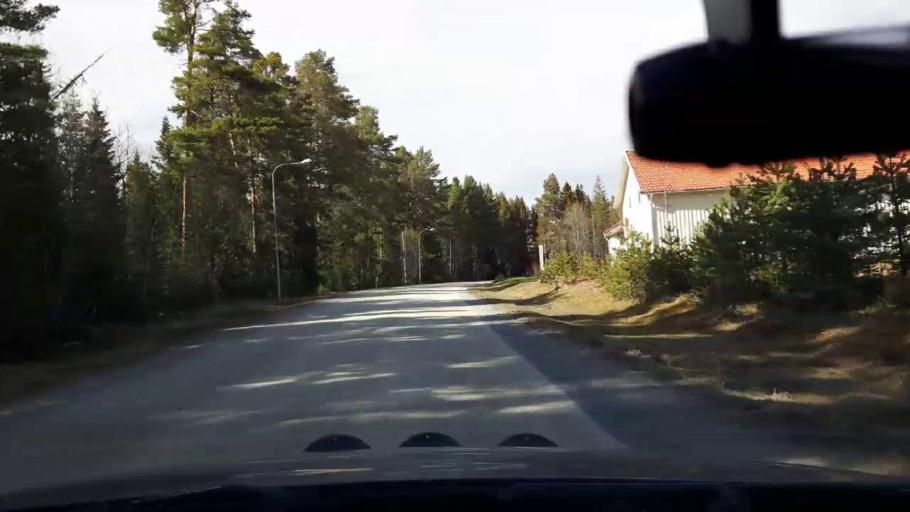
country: SE
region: Jaemtland
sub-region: Bergs Kommun
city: Hoverberg
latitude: 62.9049
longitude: 14.3406
